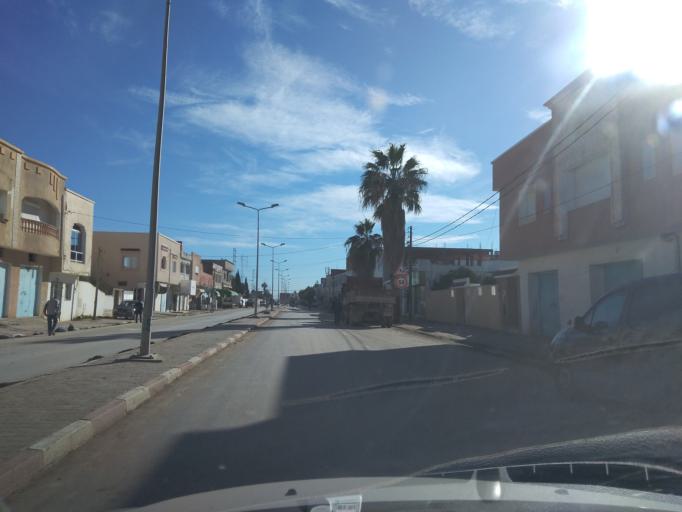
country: TN
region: Ariana
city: Qal'at al Andalus
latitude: 37.0591
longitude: 10.1195
